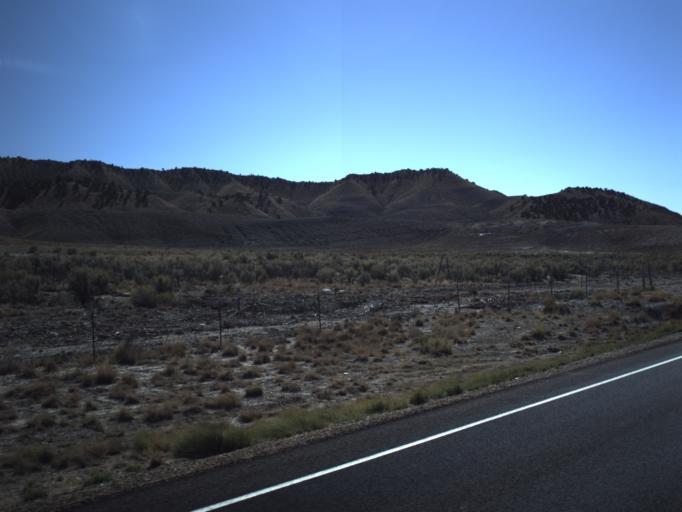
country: US
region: Utah
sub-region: Garfield County
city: Panguitch
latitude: 37.6009
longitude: -111.9699
